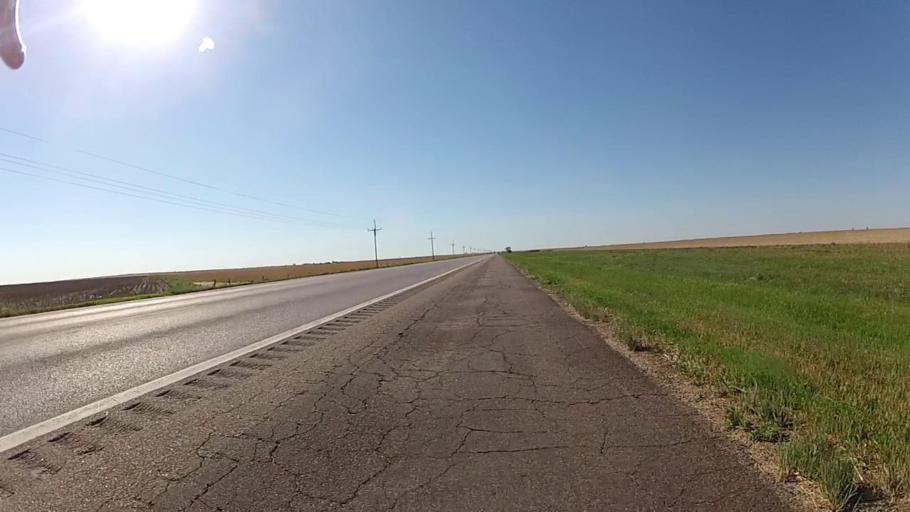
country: US
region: Kansas
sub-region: Ford County
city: Dodge City
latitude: 37.6014
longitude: -99.7023
